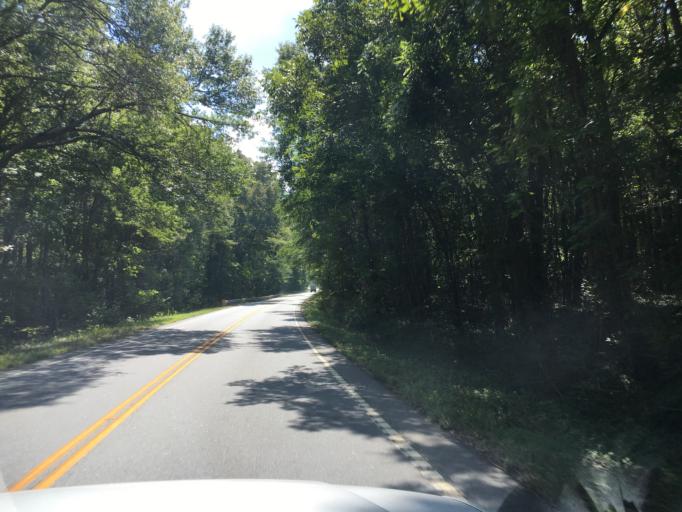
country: US
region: South Carolina
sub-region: Spartanburg County
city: Woodruff
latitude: 34.6891
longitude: -82.0641
